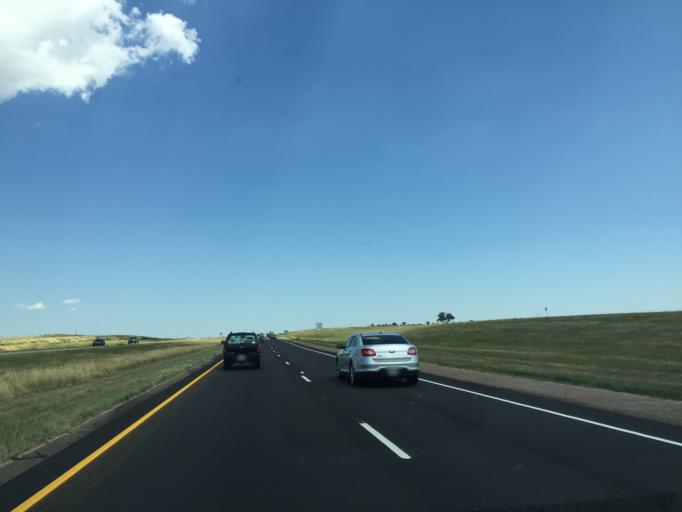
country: US
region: Colorado
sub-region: Lincoln County
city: Hugo
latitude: 39.2795
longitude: -103.3841
